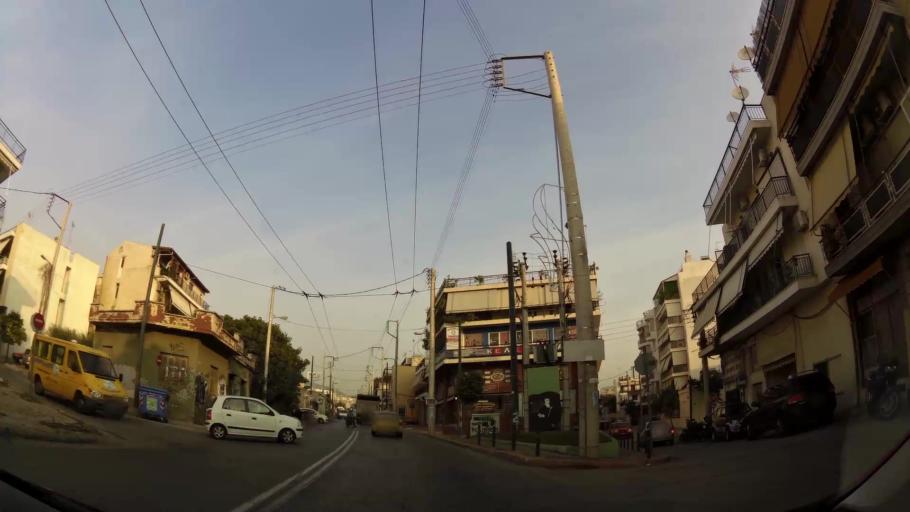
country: GR
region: Attica
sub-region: Nomarchia Athinas
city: Peristeri
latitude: 38.0224
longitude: 23.6850
